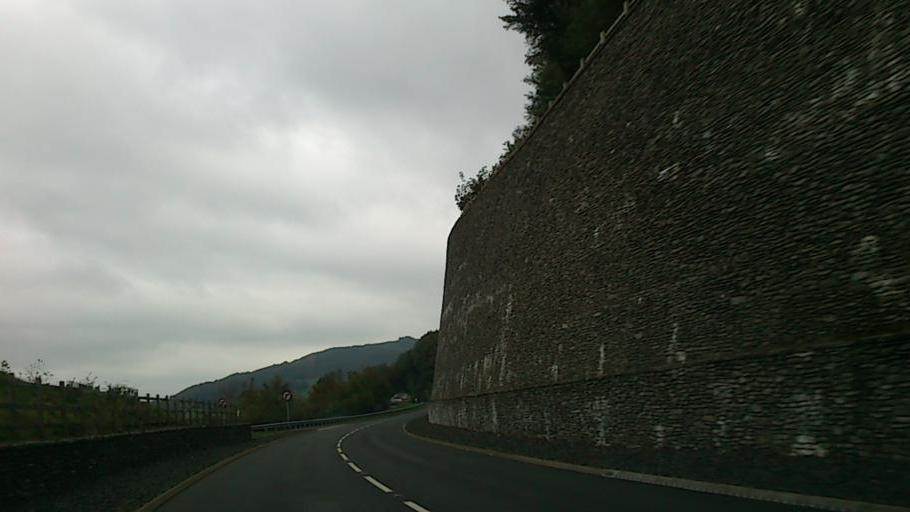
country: GB
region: Wales
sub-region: Sir Powys
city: Machynlleth
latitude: 52.5525
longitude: -3.9316
